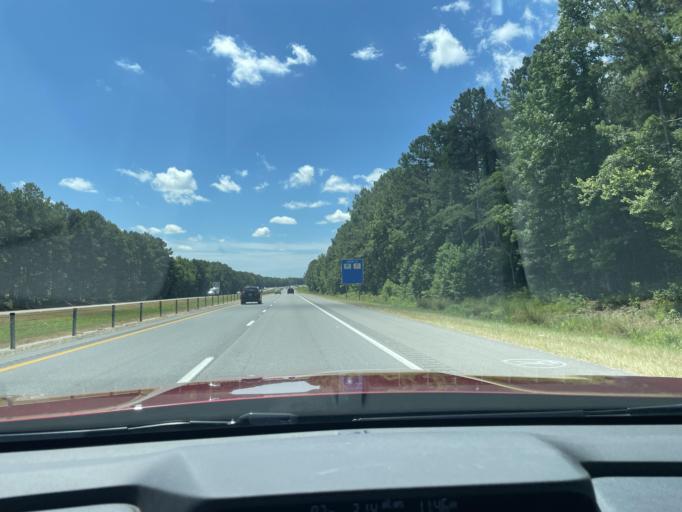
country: US
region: Arkansas
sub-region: Jefferson County
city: White Hall
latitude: 34.2740
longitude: -92.1111
